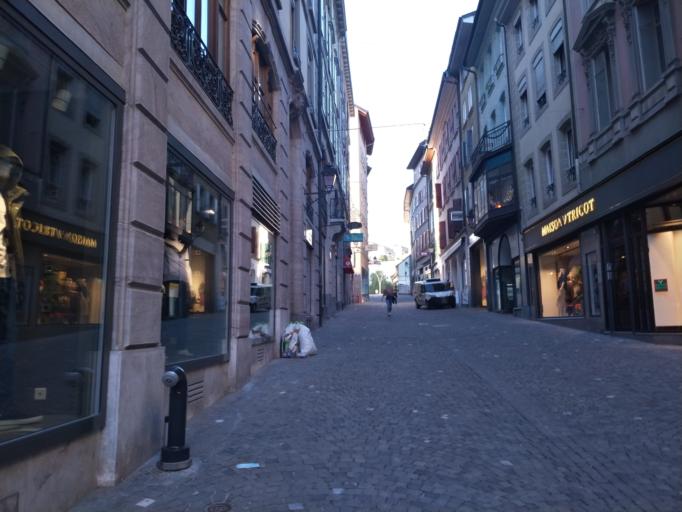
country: CH
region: Vaud
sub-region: Lausanne District
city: Lausanne
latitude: 46.5221
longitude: 6.6328
